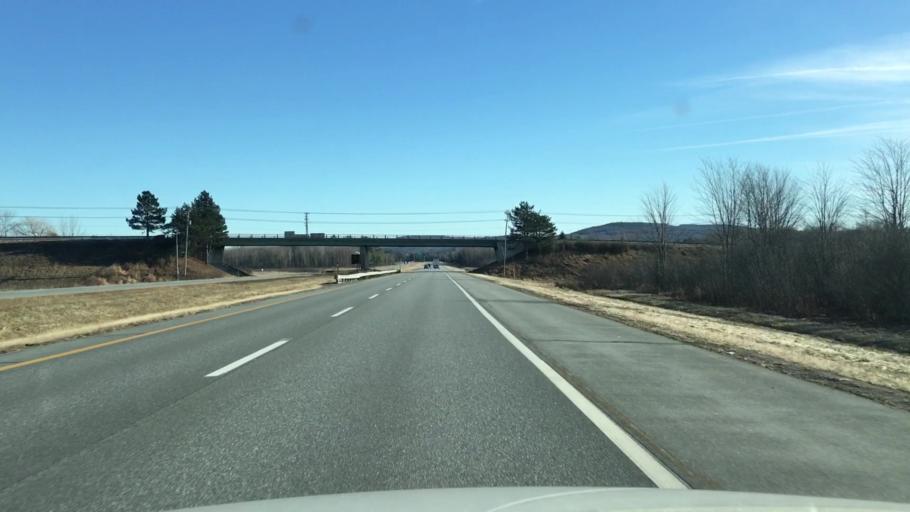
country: US
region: Maine
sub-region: Penobscot County
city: Brewer
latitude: 44.7748
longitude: -68.7480
